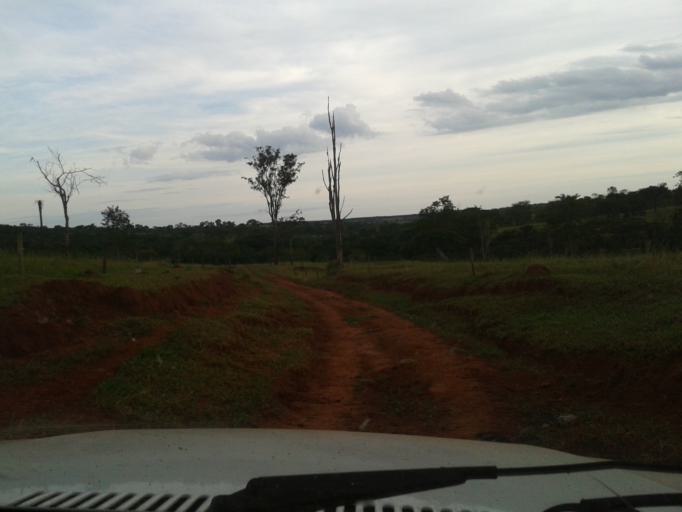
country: BR
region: Minas Gerais
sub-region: Campina Verde
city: Campina Verde
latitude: -19.4136
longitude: -49.6040
